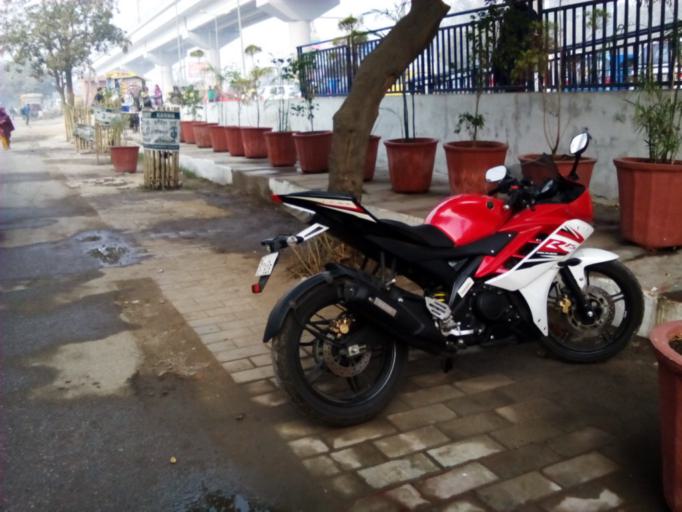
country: IN
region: Uttar Pradesh
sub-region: Gautam Buddha Nagar
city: Noida
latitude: 28.6451
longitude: 77.3238
